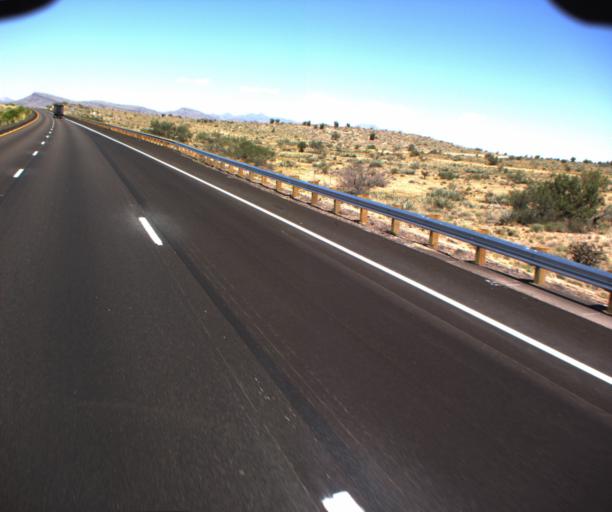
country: US
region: Arizona
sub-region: Mohave County
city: Peach Springs
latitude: 35.1613
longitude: -113.5726
